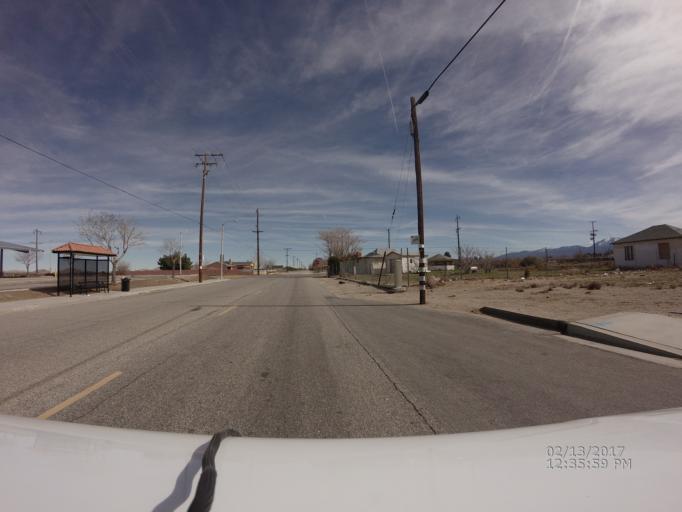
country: US
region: California
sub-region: Los Angeles County
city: Littlerock
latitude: 34.5727
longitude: -117.9349
